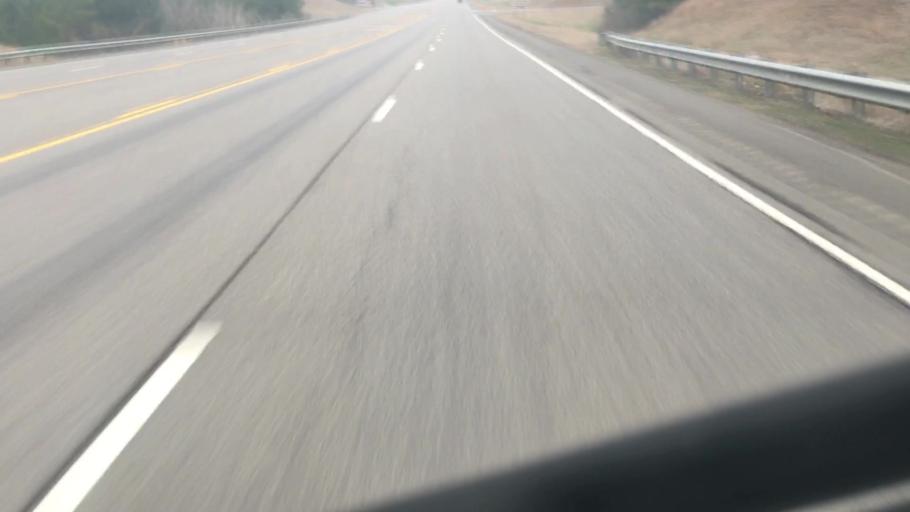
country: US
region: Alabama
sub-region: Walker County
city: Jasper
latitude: 33.8050
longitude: -87.2351
